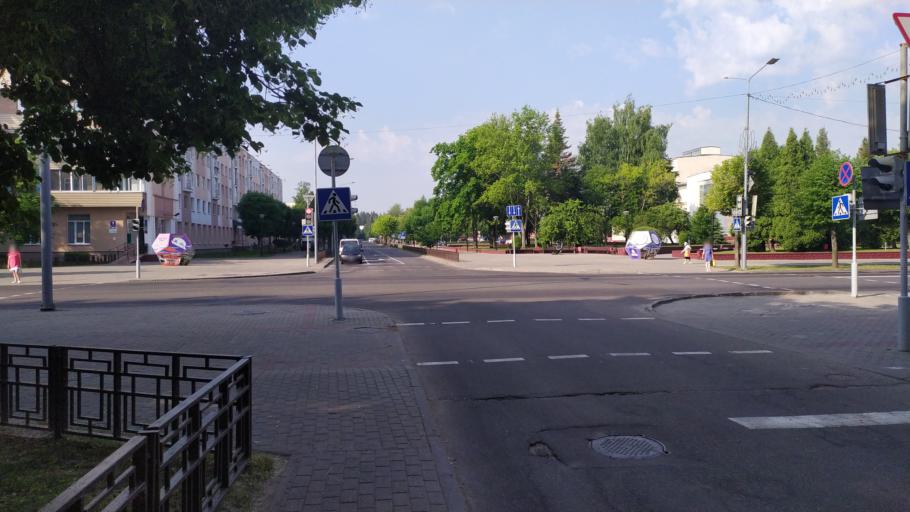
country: BY
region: Vitebsk
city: Navapolatsk
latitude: 55.5351
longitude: 28.6490
